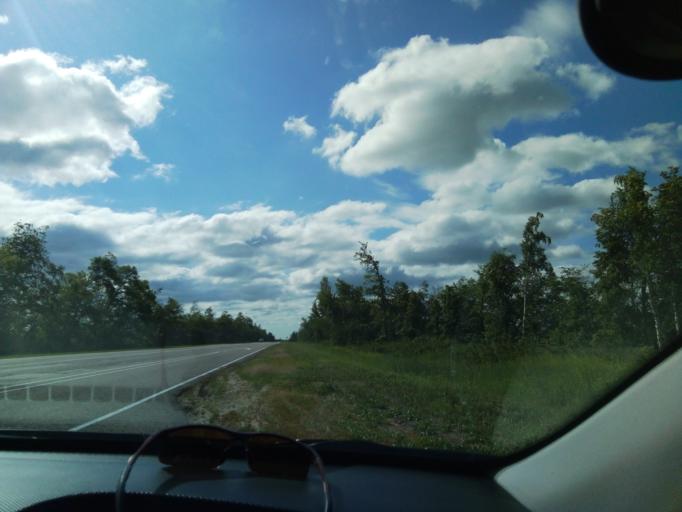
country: RU
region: Tambov
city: Morshansk
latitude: 53.5609
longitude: 41.7681
